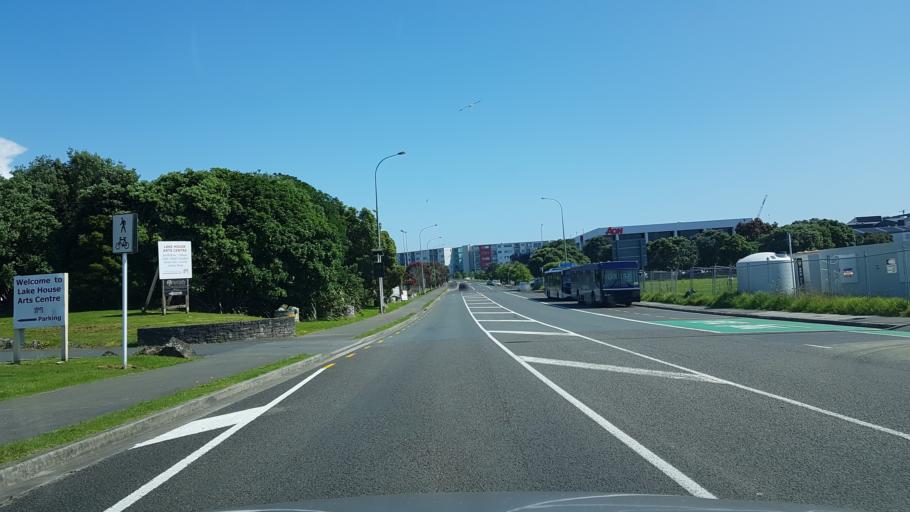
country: NZ
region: Auckland
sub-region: Auckland
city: North Shore
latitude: -36.7943
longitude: 174.7632
